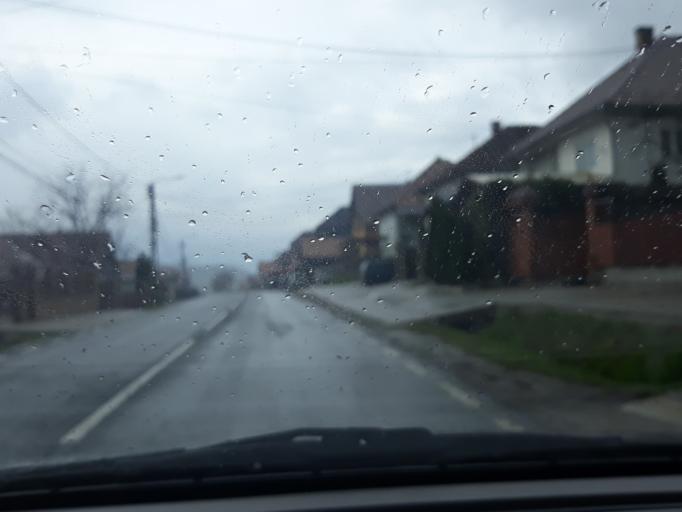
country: RO
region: Harghita
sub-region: Comuna Corund
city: Corund
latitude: 46.4769
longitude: 25.1760
